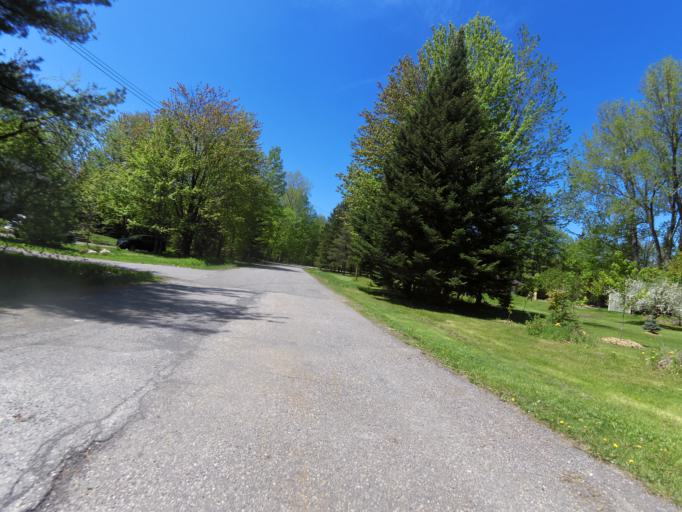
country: CA
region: Ontario
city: Ottawa
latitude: 45.4153
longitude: -75.7853
